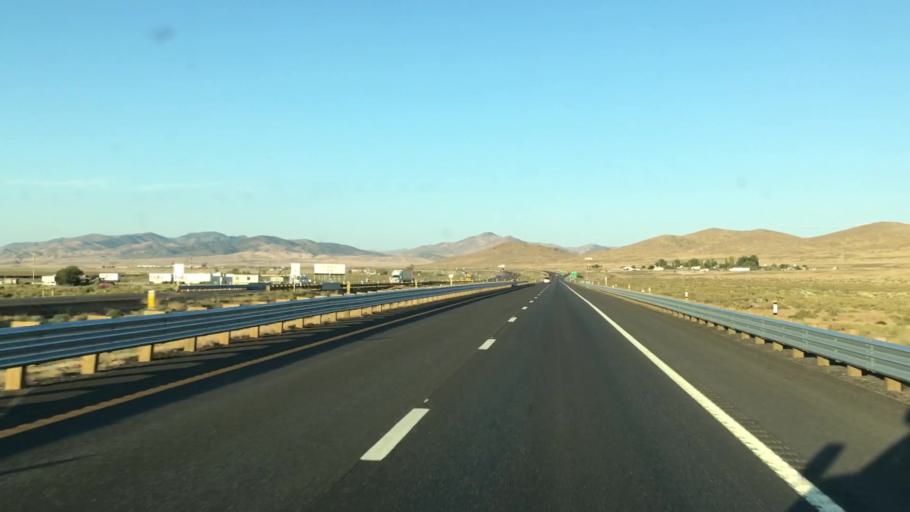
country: US
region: Nevada
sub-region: Humboldt County
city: Winnemucca
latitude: 40.6750
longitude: -118.0816
